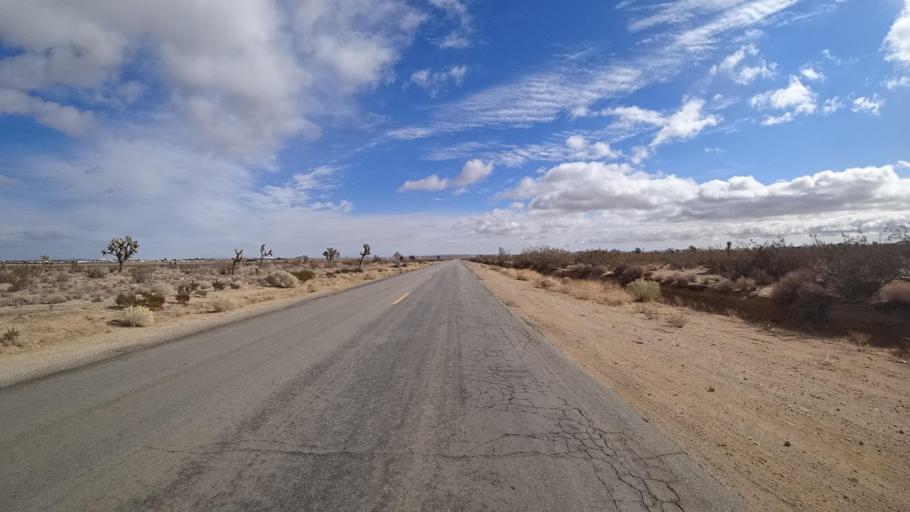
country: US
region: California
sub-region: Kern County
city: Mojave
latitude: 35.0317
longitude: -118.1844
